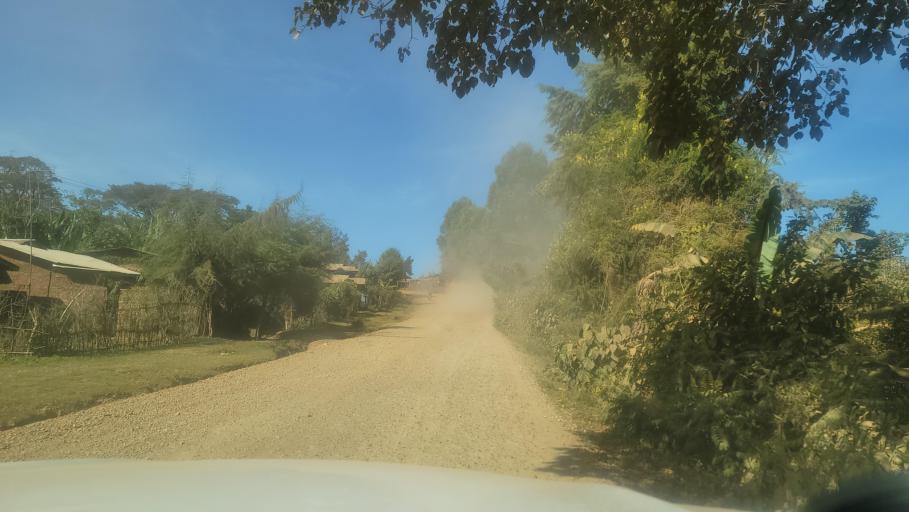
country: ET
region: Oromiya
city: Agaro
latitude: 7.8149
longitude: 36.5089
